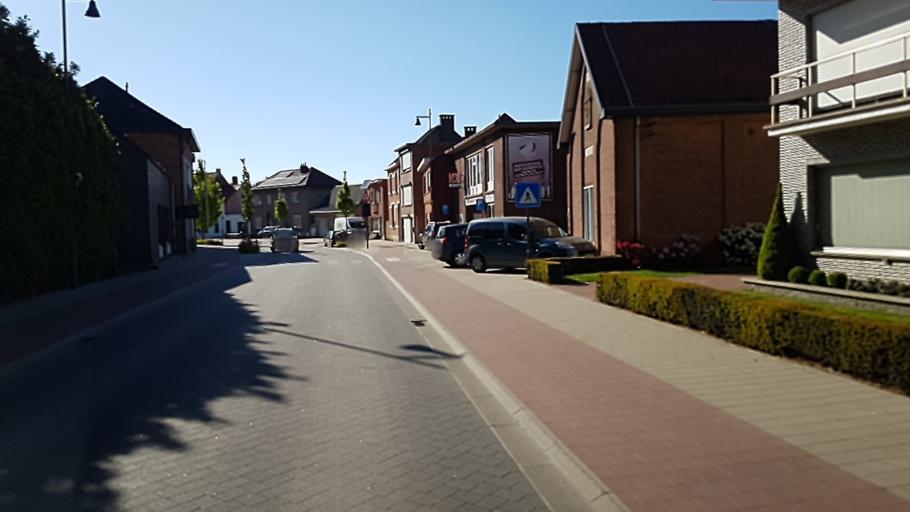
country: BE
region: Flanders
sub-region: Provincie Antwerpen
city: Heist-op-den-Berg
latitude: 51.1035
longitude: 4.7262
